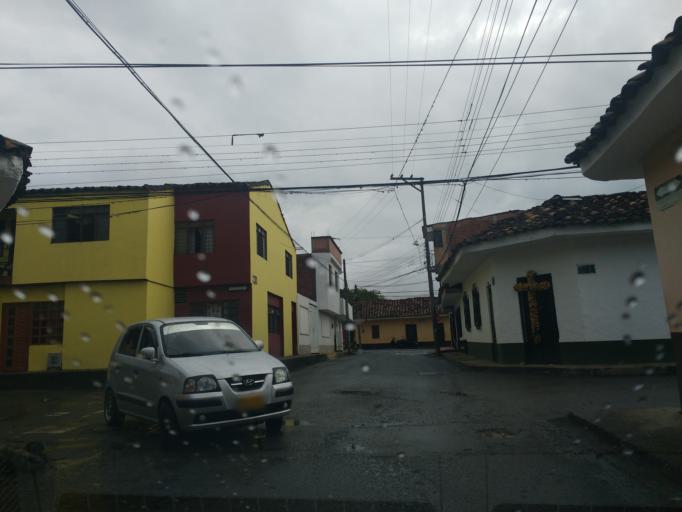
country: CO
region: Cauca
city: Santander de Quilichao
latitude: 3.0033
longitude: -76.4812
